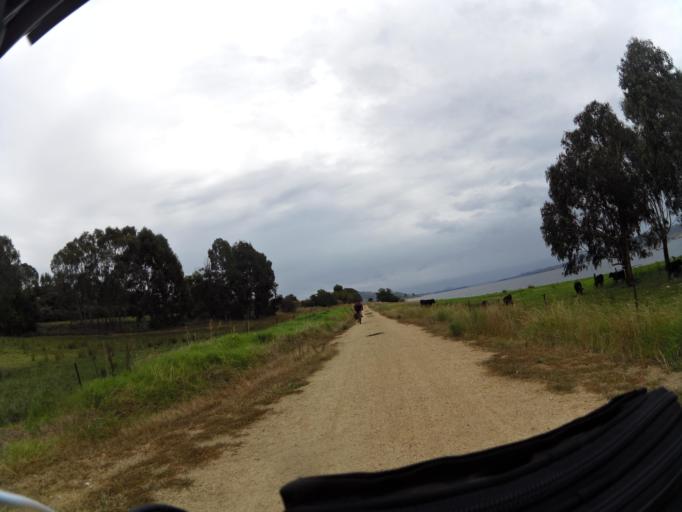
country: AU
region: New South Wales
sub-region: Albury Municipality
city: East Albury
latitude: -36.2243
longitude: 147.0744
